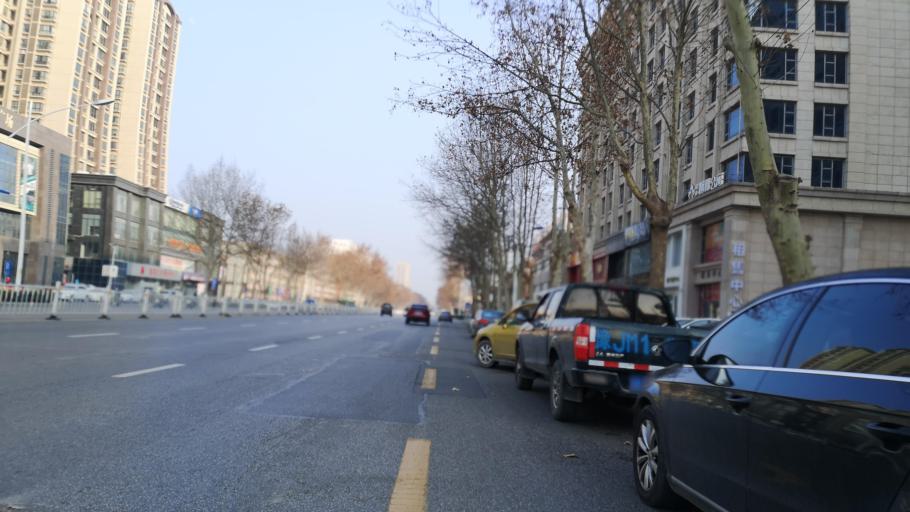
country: CN
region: Henan Sheng
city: Zhongyuanlu
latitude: 35.7797
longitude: 115.0498
